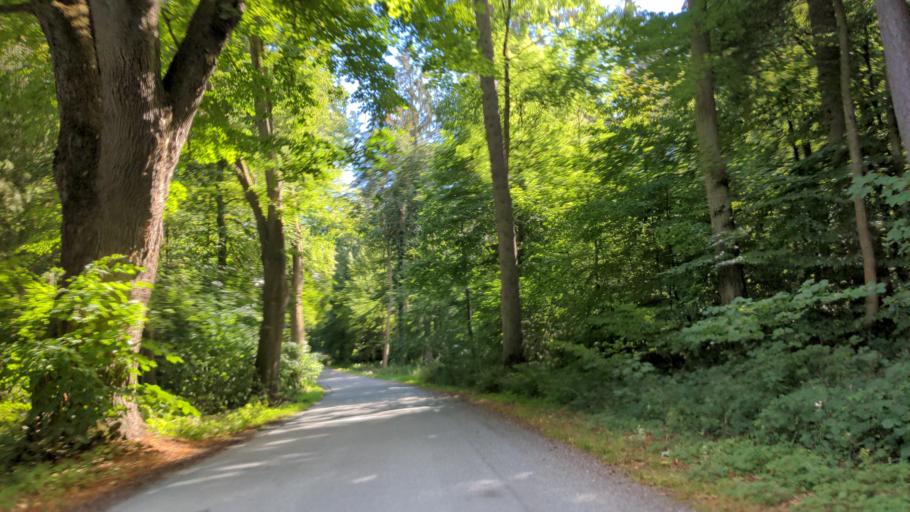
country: DE
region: Schleswig-Holstein
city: Kasseedorf
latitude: 54.1518
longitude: 10.7230
